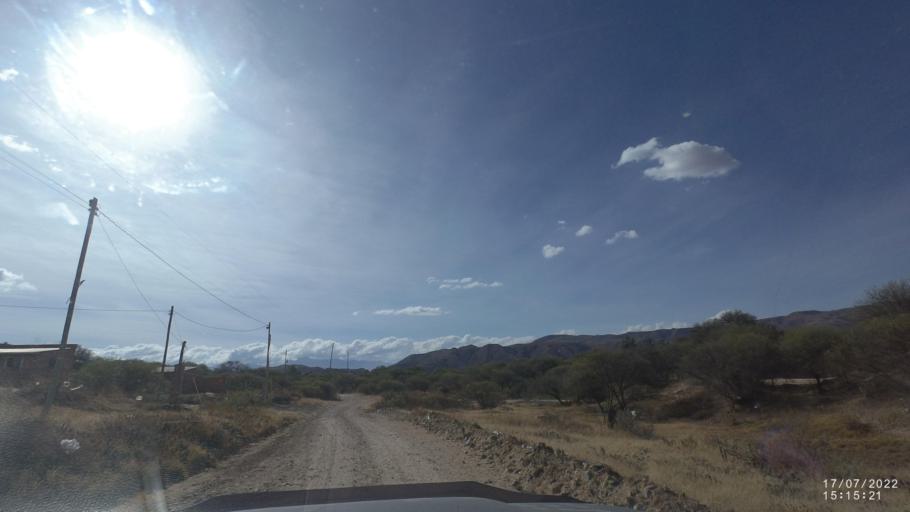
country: BO
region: Cochabamba
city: Capinota
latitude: -17.5574
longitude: -66.2621
